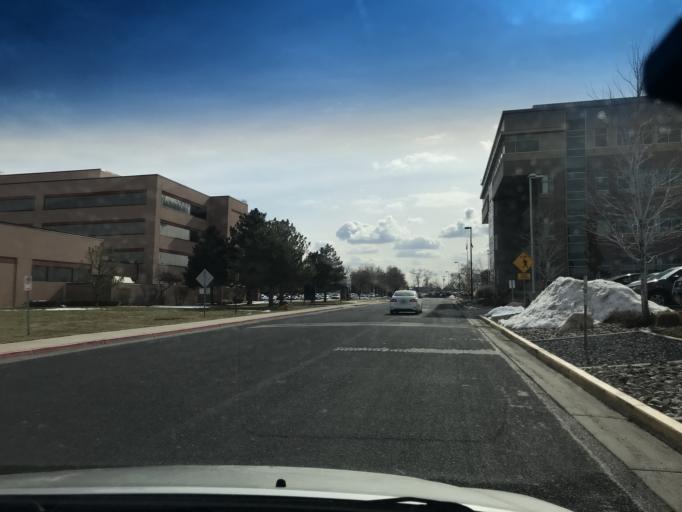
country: US
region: Utah
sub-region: Salt Lake County
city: Salt Lake City
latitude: 40.7754
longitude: -111.9475
